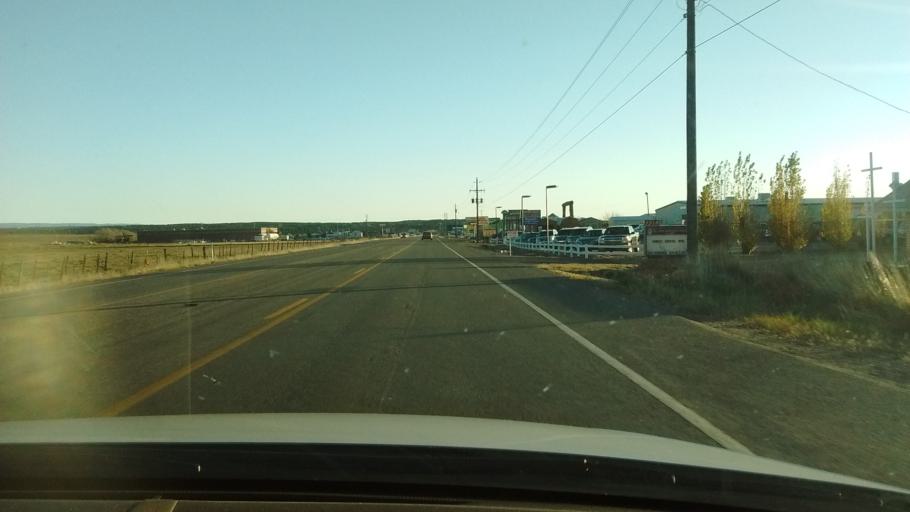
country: US
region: Utah
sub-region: Kane County
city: Kanab
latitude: 37.0222
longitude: -112.5249
